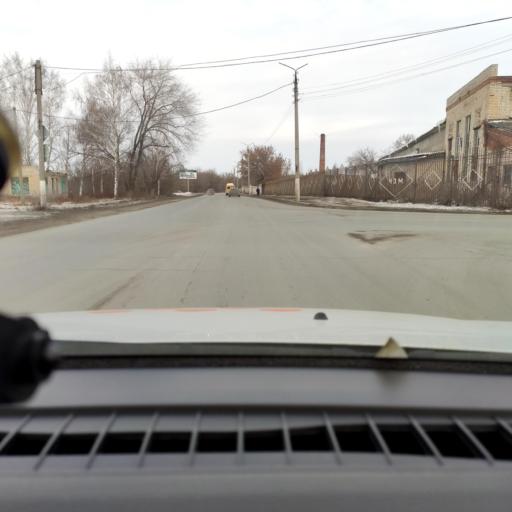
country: RU
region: Samara
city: Chapayevsk
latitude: 52.9658
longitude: 49.6935
